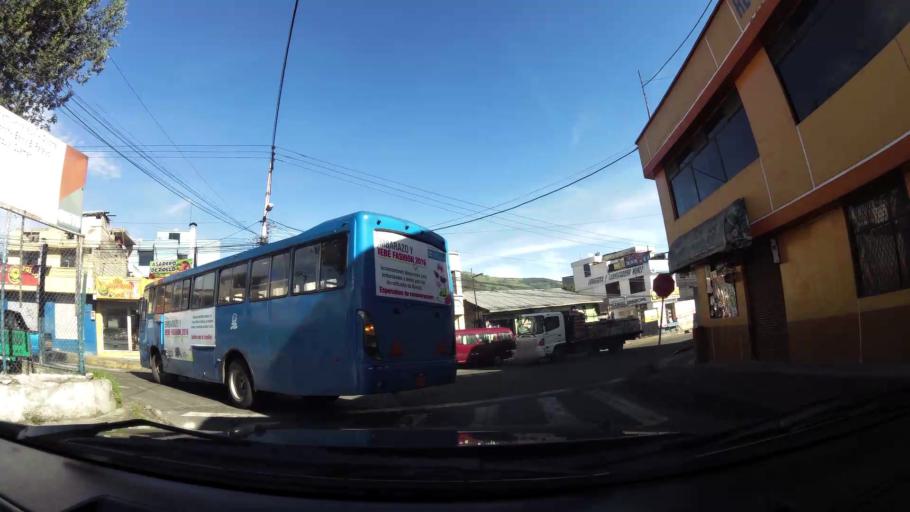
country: EC
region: Pichincha
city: Sangolqui
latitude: -0.3318
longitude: -78.5550
